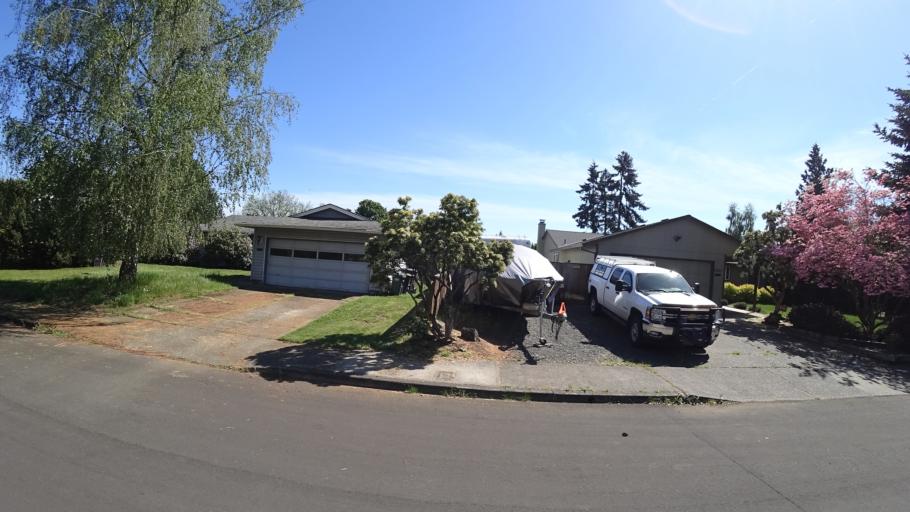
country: US
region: Oregon
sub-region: Washington County
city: Hillsboro
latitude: 45.5170
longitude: -122.9518
